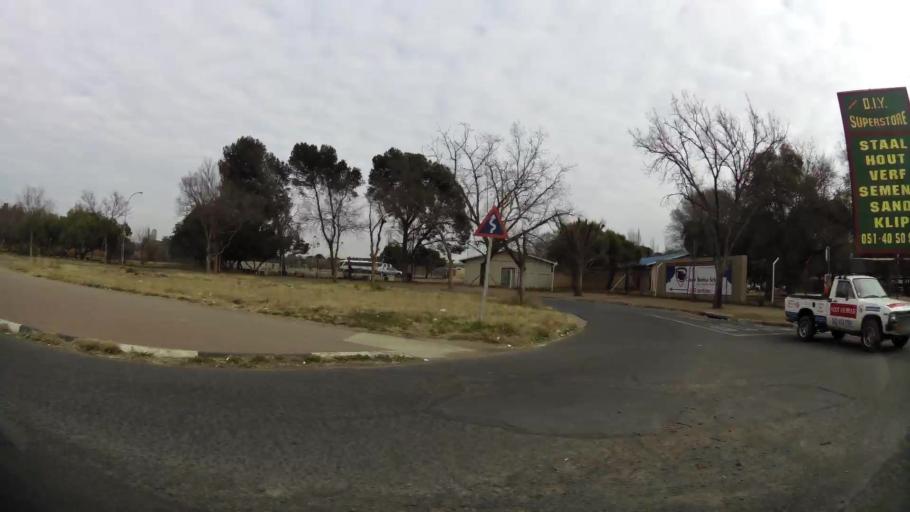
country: ZA
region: Orange Free State
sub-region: Mangaung Metropolitan Municipality
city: Bloemfontein
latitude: -29.1312
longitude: 26.2074
